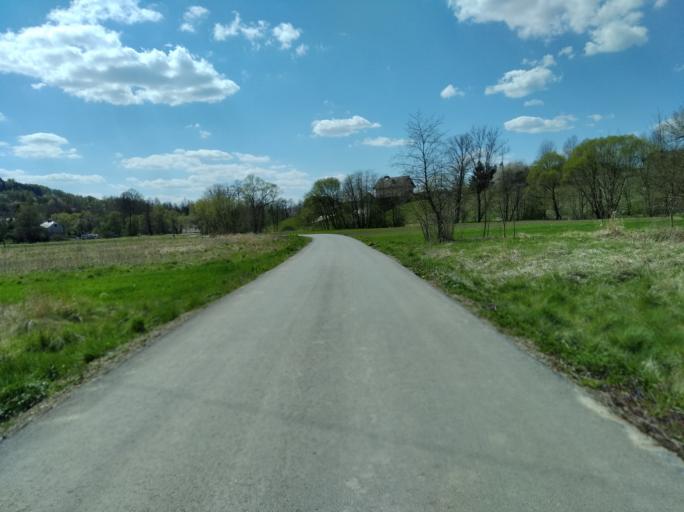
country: PL
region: Subcarpathian Voivodeship
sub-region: Powiat brzozowski
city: Domaradz
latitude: 49.7905
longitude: 21.9705
